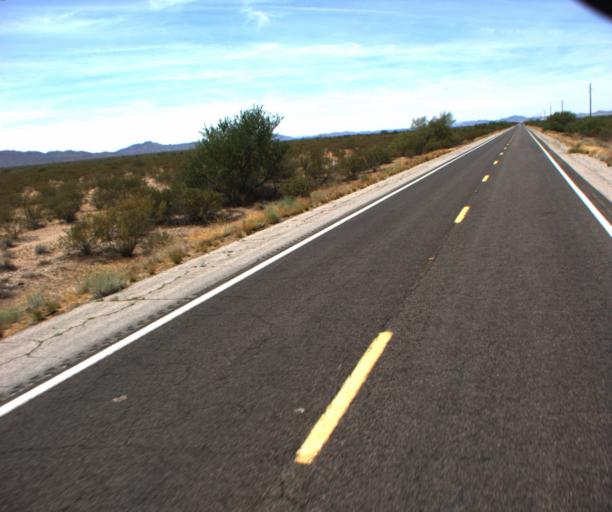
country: US
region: Arizona
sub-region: La Paz County
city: Salome
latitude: 33.8589
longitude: -113.4259
